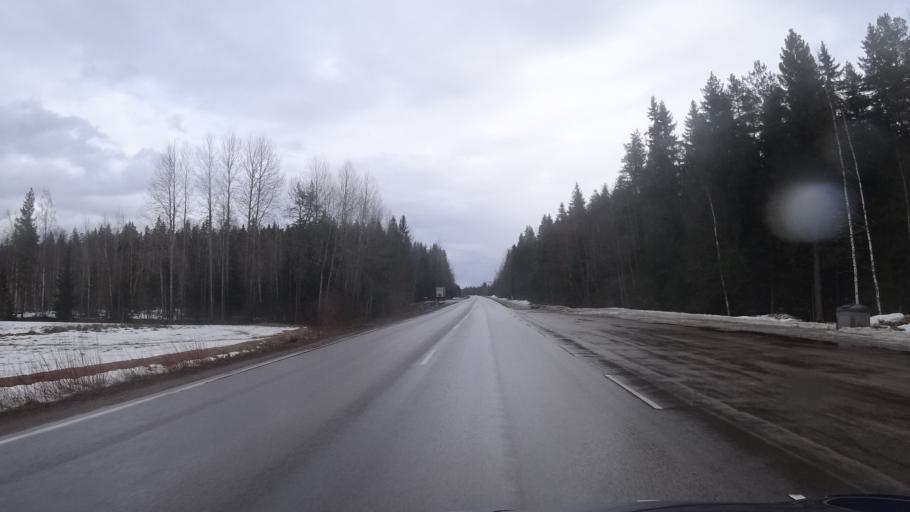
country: FI
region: Kymenlaakso
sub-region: Kouvola
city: Elimaeki
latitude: 60.6904
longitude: 26.5763
